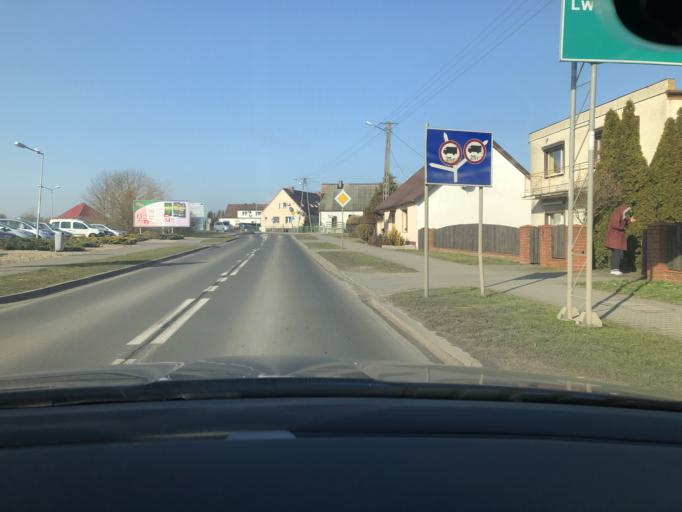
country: PL
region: Greater Poland Voivodeship
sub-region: Powiat szamotulski
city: Duszniki
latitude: 52.4520
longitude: 16.4012
